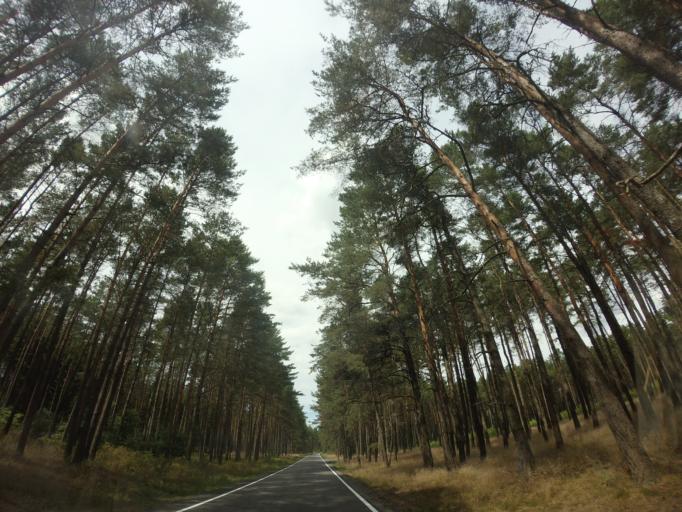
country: PL
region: West Pomeranian Voivodeship
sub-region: Powiat choszczenski
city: Drawno
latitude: 53.1304
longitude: 15.7237
